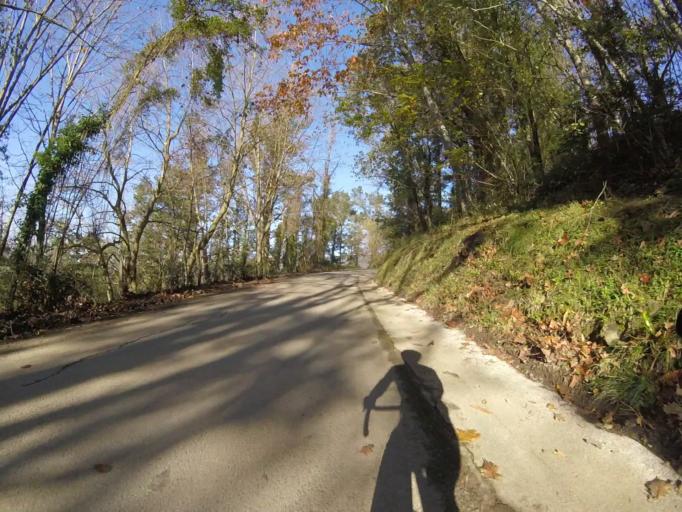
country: ES
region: Basque Country
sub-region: Provincia de Guipuzcoa
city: Usurbil
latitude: 43.2784
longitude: -2.0698
